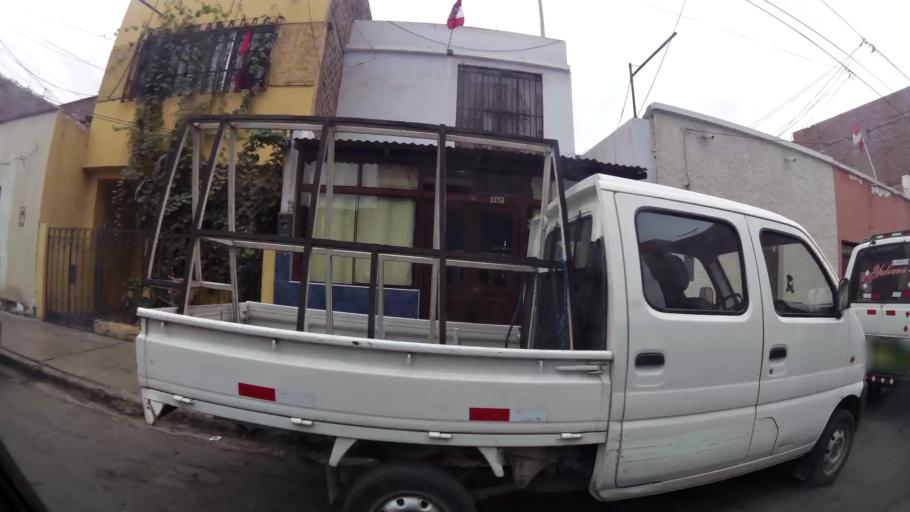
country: PE
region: La Libertad
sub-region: Provincia de Trujillo
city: Trujillo
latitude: -8.1143
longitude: -79.0206
